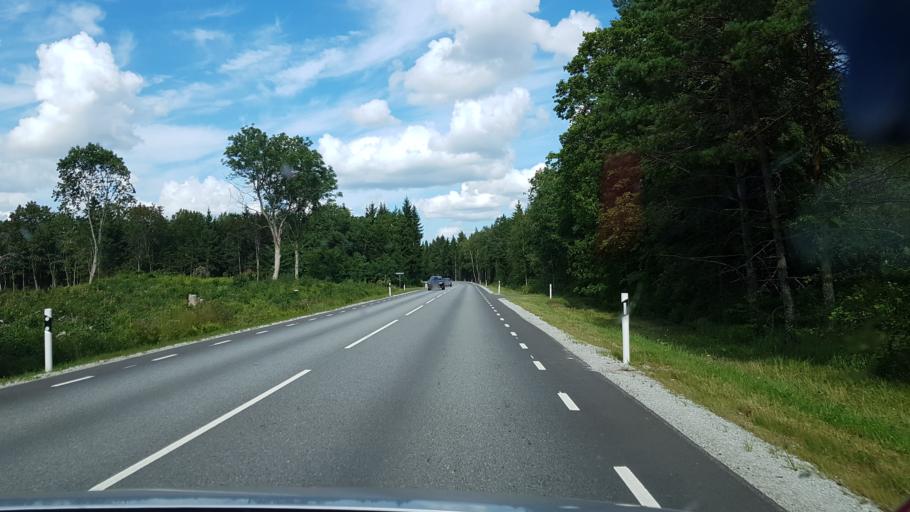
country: EE
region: Harju
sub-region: Nissi vald
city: Turba
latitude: 59.0707
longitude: 23.9108
